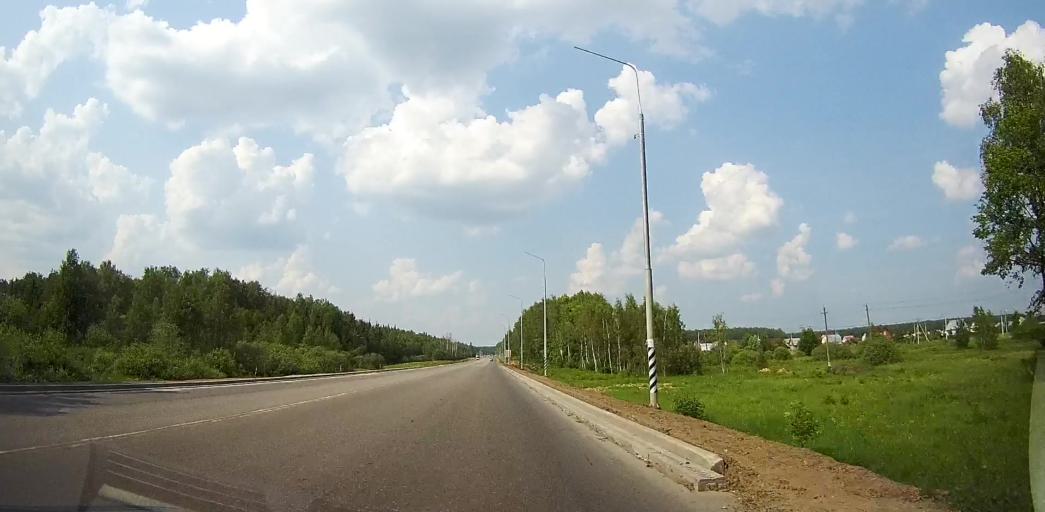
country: RU
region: Moskovskaya
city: Mikhnevo
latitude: 55.0617
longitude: 37.9543
